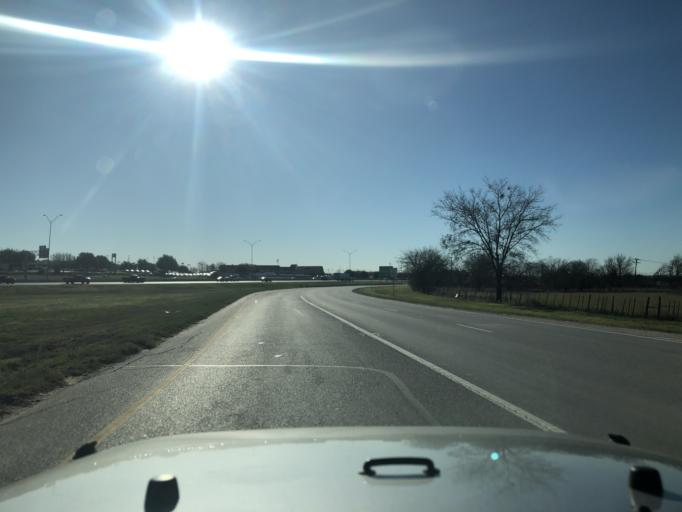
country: US
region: Texas
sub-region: Williamson County
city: Georgetown
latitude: 30.5763
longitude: -97.6941
